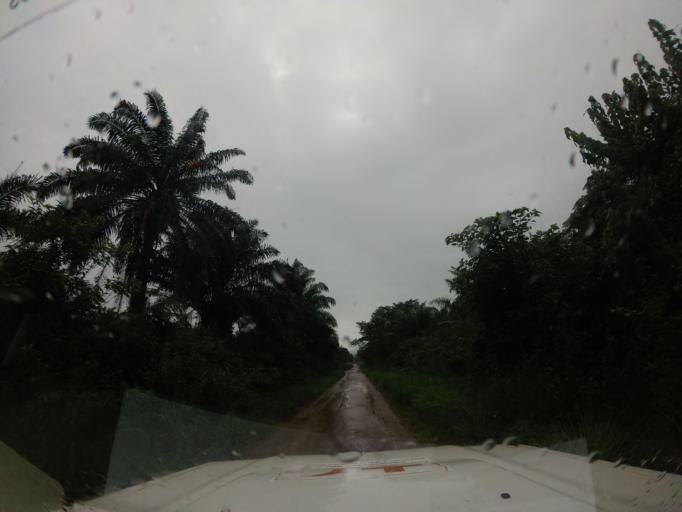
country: SL
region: Eastern Province
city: Kenema
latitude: 7.7544
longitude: -11.1971
